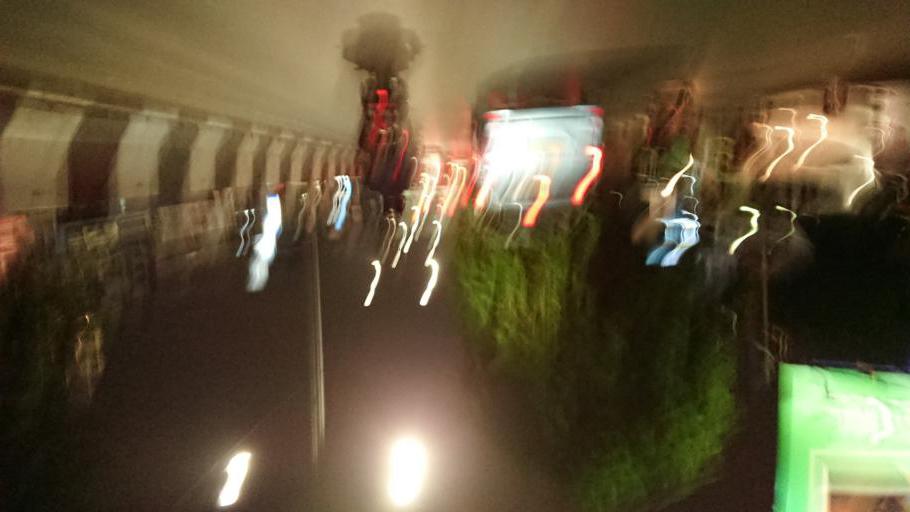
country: ID
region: Jakarta Raya
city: Jakarta
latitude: -6.1910
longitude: 106.8151
